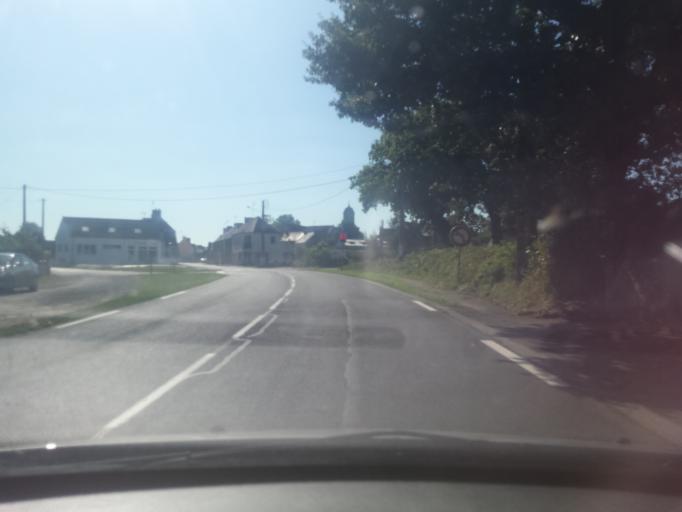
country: FR
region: Brittany
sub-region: Departement des Cotes-d'Armor
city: Plounevez-Quintin
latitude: 48.2917
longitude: -3.2291
